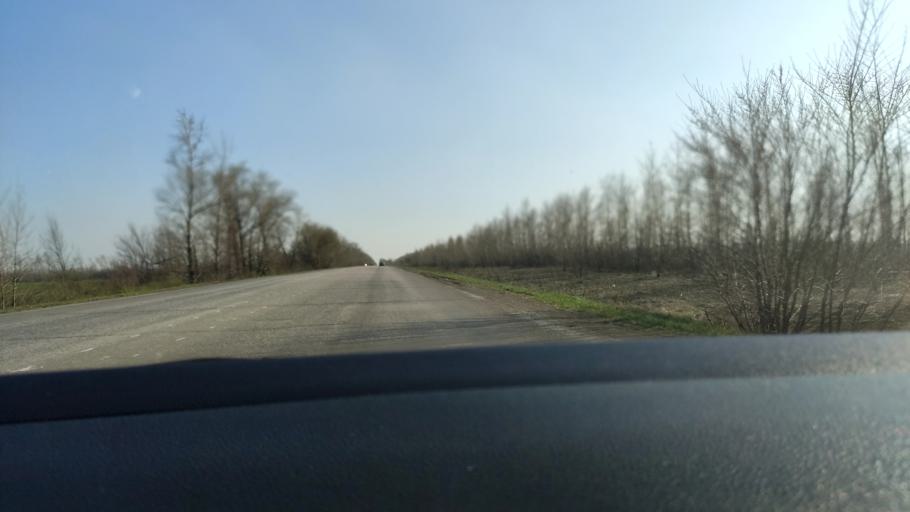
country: RU
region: Voronezj
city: Maslovka
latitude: 51.4974
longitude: 39.3086
